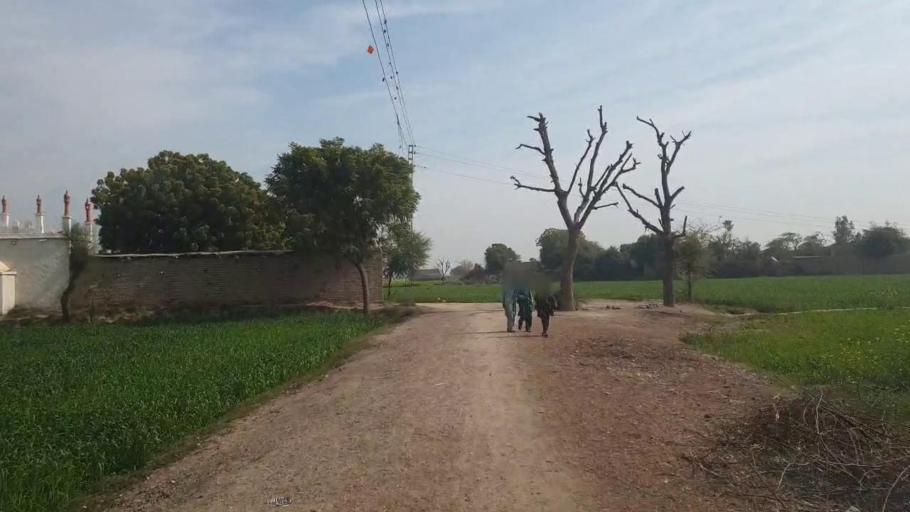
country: PK
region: Sindh
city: Nawabshah
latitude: 26.1277
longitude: 68.4977
